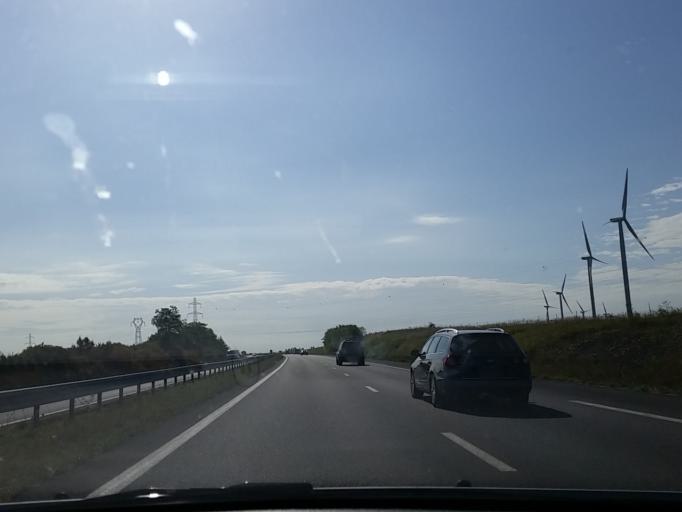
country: FR
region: Centre
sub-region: Departement du Cher
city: Mehun-sur-Yevre
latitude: 47.1054
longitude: 2.2132
